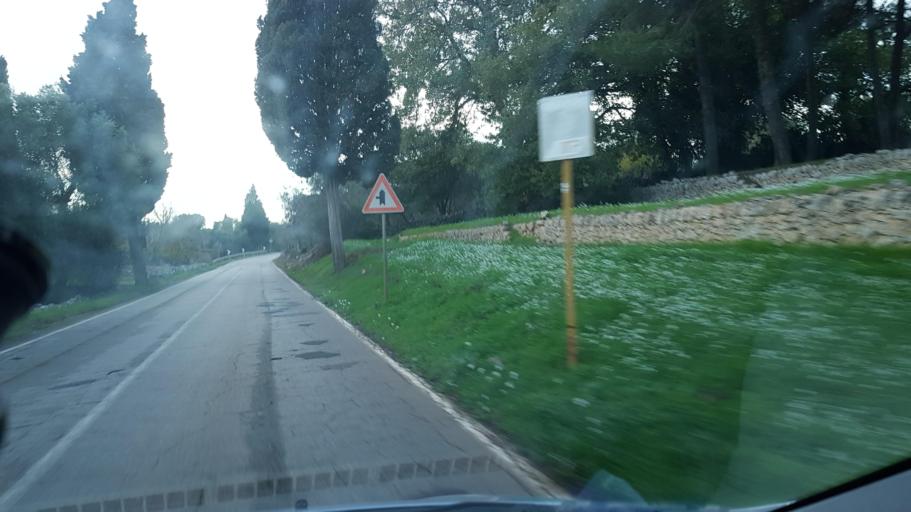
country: IT
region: Apulia
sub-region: Provincia di Brindisi
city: San Michele Salentino
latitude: 40.6413
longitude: 17.5790
